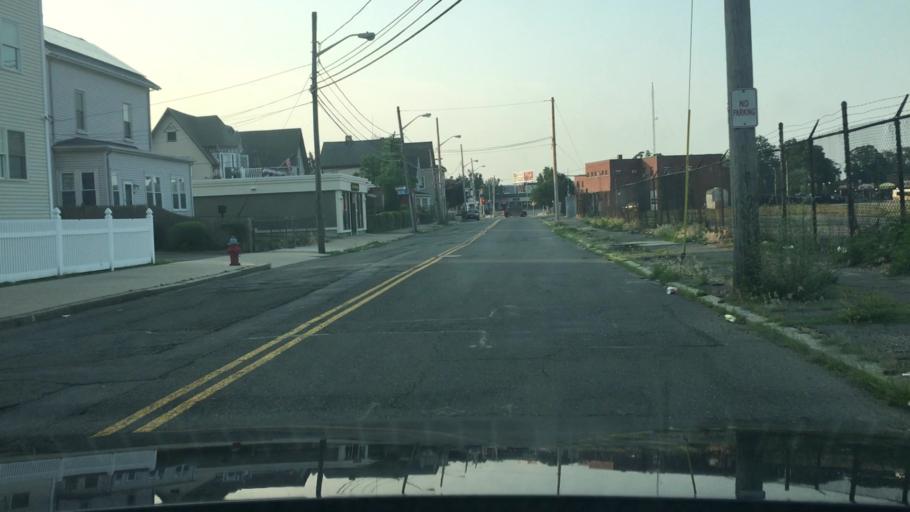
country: US
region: Massachusetts
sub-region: Essex County
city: Lynn
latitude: 42.4649
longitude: -70.9660
